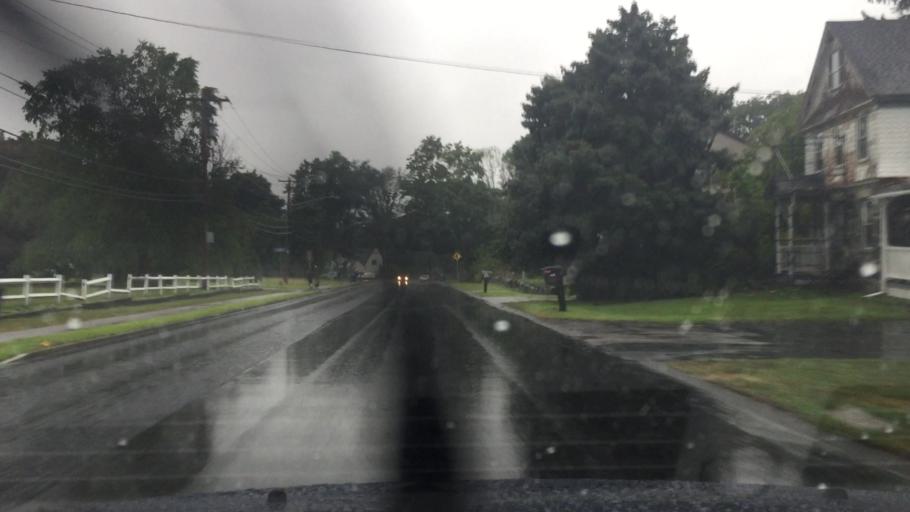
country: US
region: Massachusetts
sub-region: Middlesex County
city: Tewksbury
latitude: 42.6421
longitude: -71.2482
